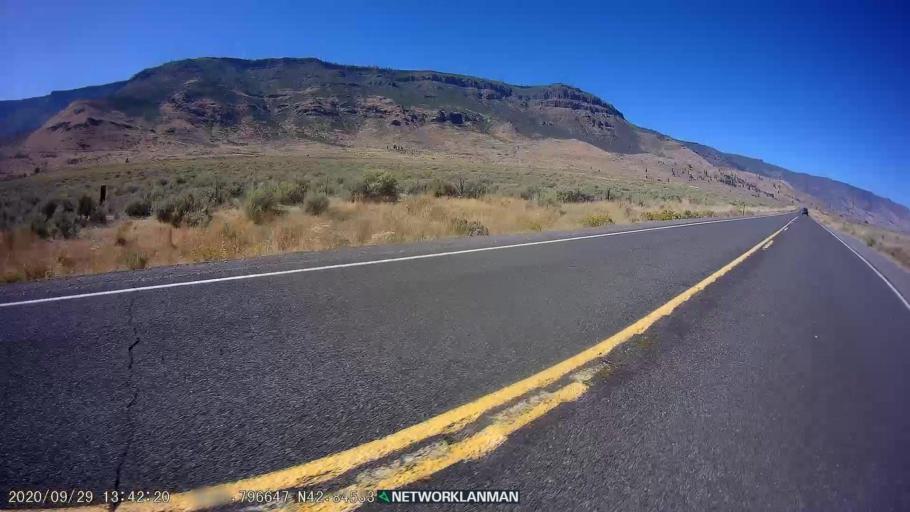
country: US
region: Oregon
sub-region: Lake County
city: Lakeview
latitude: 42.8455
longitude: -120.7968
